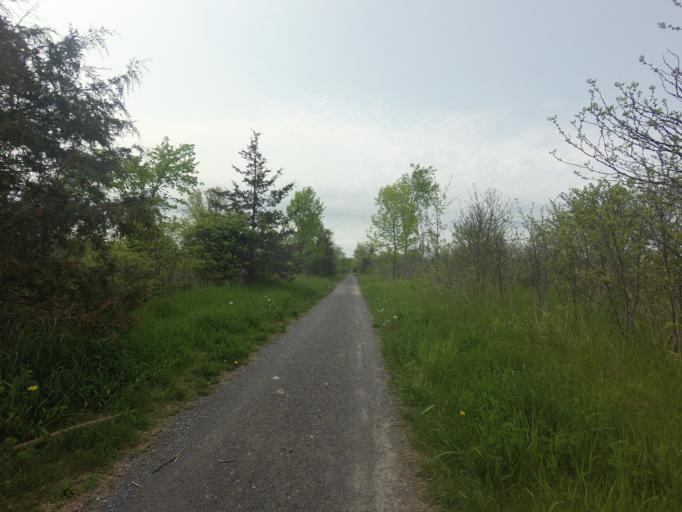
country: CA
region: Ontario
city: Kingston
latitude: 44.3155
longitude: -76.5853
